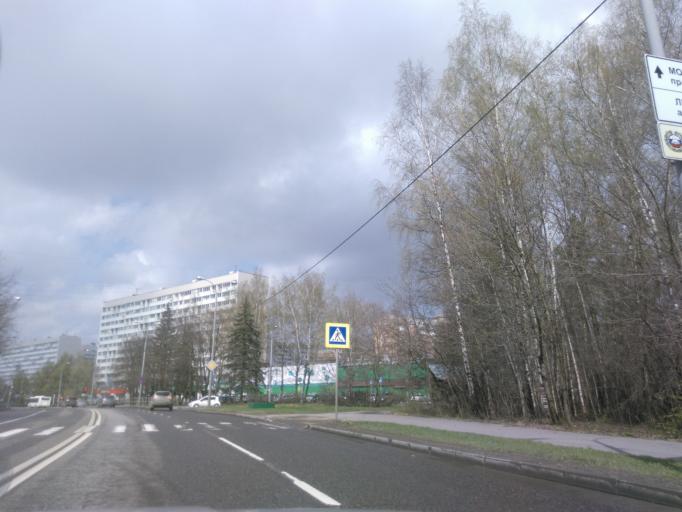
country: RU
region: Moskovskaya
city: Rzhavki
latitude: 55.9869
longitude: 37.2349
